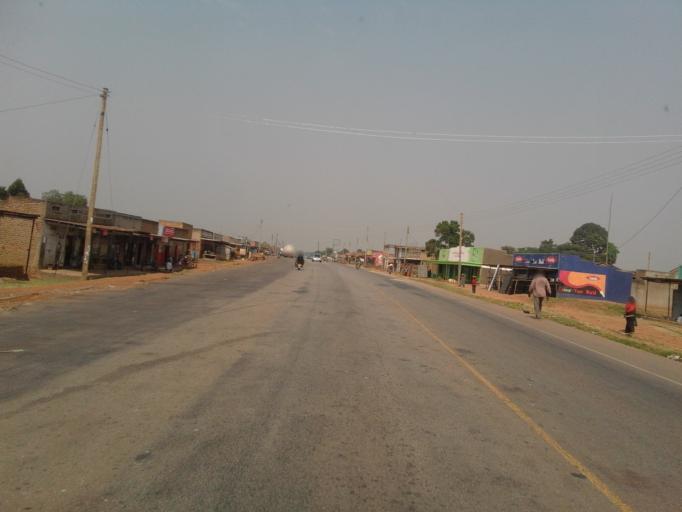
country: UG
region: Eastern Region
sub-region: Bugiri District
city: Bugiri
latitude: 0.6224
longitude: 33.6262
